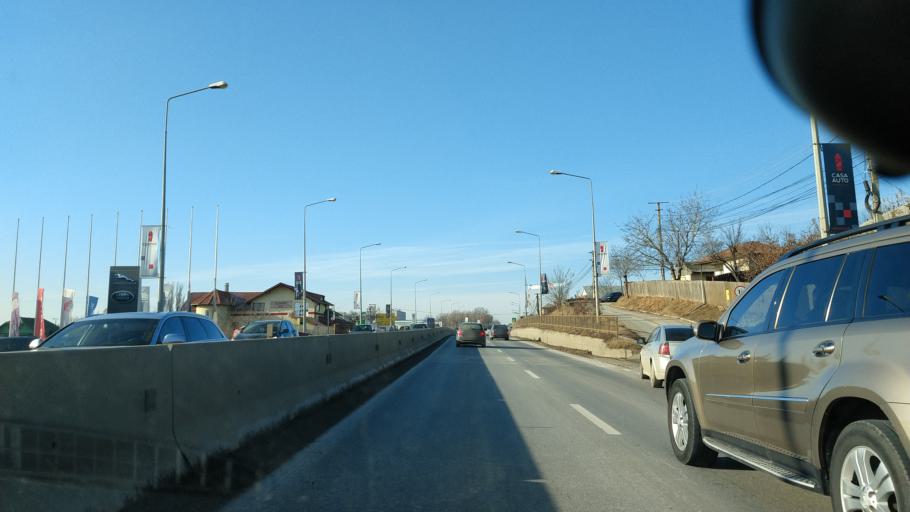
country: RO
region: Iasi
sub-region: Comuna Valea Lupului
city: Valea Lupului
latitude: 47.1748
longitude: 27.5007
